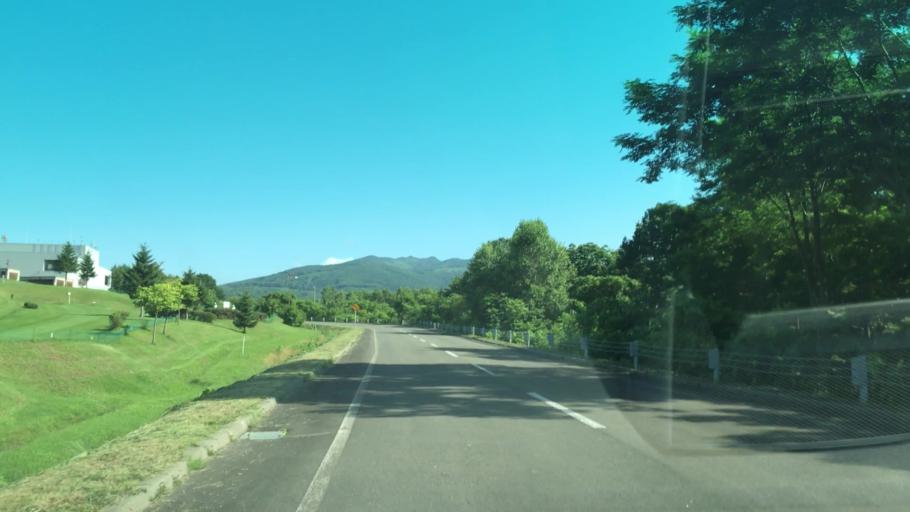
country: JP
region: Hokkaido
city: Iwanai
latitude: 42.9758
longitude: 140.6080
